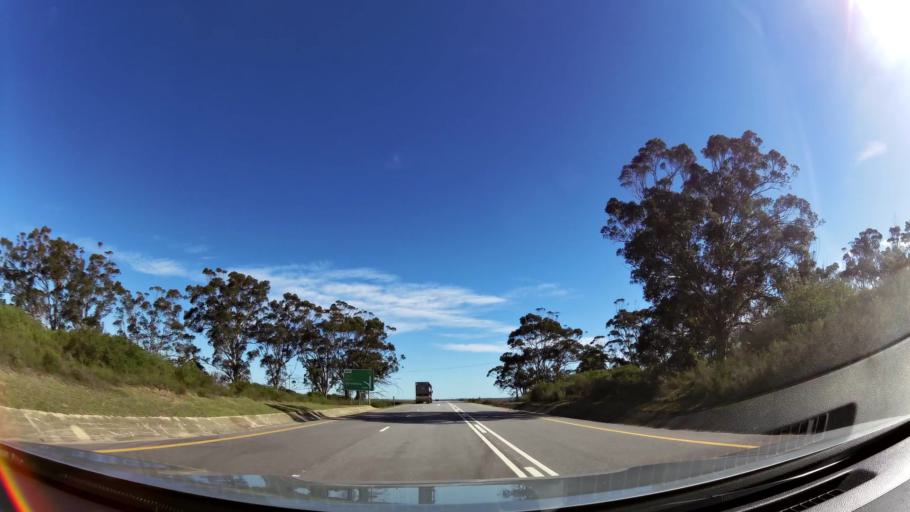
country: ZA
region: Eastern Cape
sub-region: Cacadu District Municipality
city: Kruisfontein
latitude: -34.0201
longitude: 24.6184
